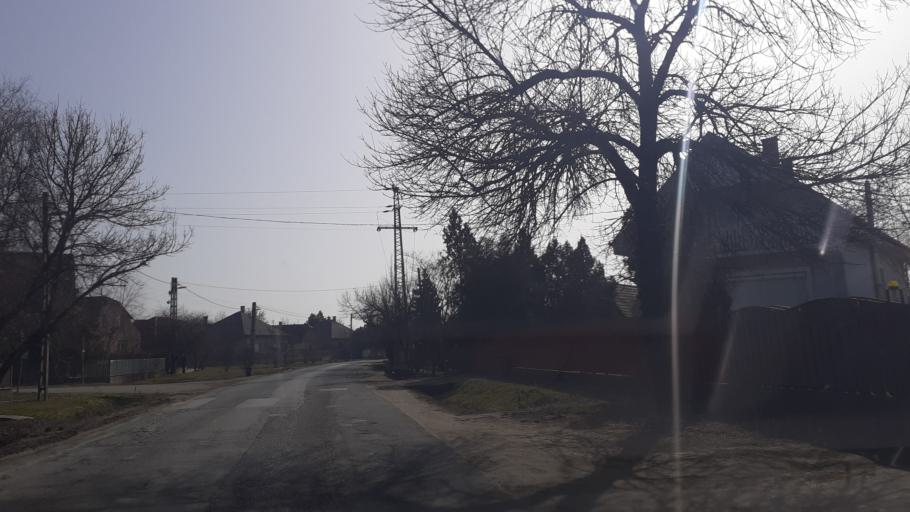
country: HU
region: Pest
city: Bugyi
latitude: 47.2188
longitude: 19.1471
